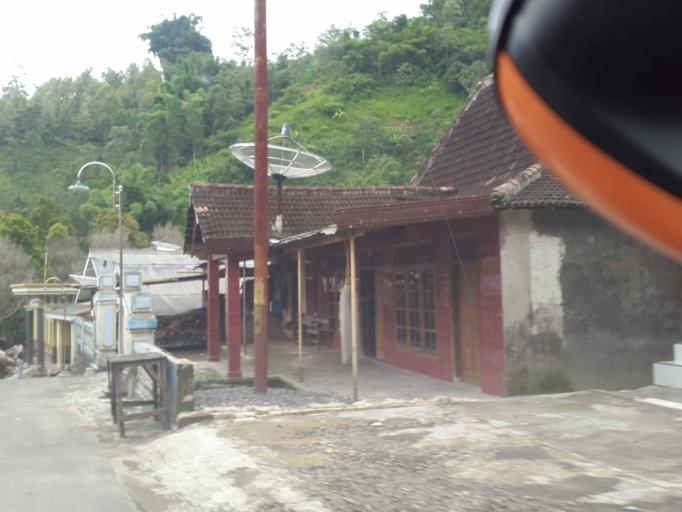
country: ID
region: Central Java
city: Jatiroto
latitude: -7.7106
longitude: 111.1288
